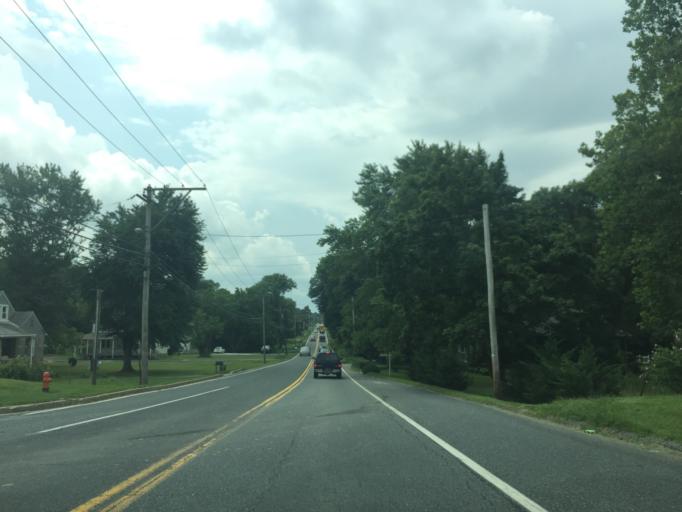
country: US
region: Maryland
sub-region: Baltimore County
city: White Marsh
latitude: 39.3892
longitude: -76.4280
